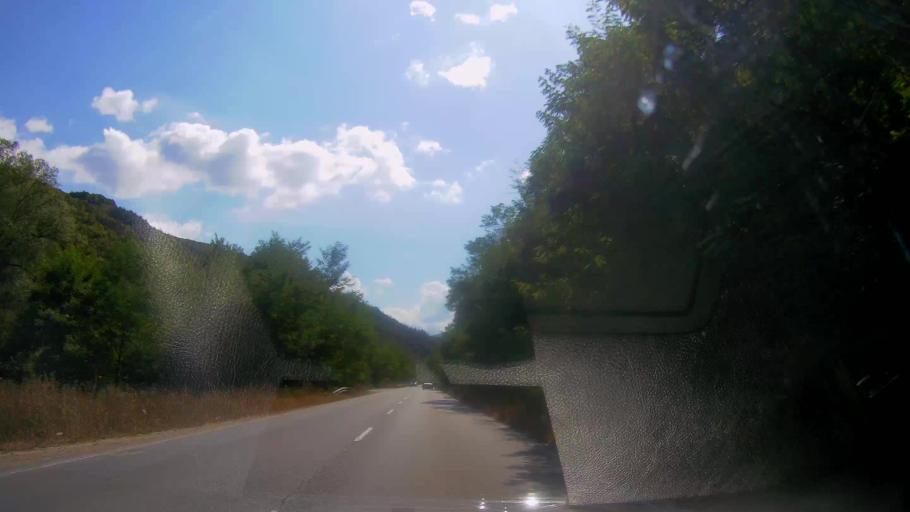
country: BG
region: Stara Zagora
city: Gurkovo
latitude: 42.7535
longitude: 25.7090
